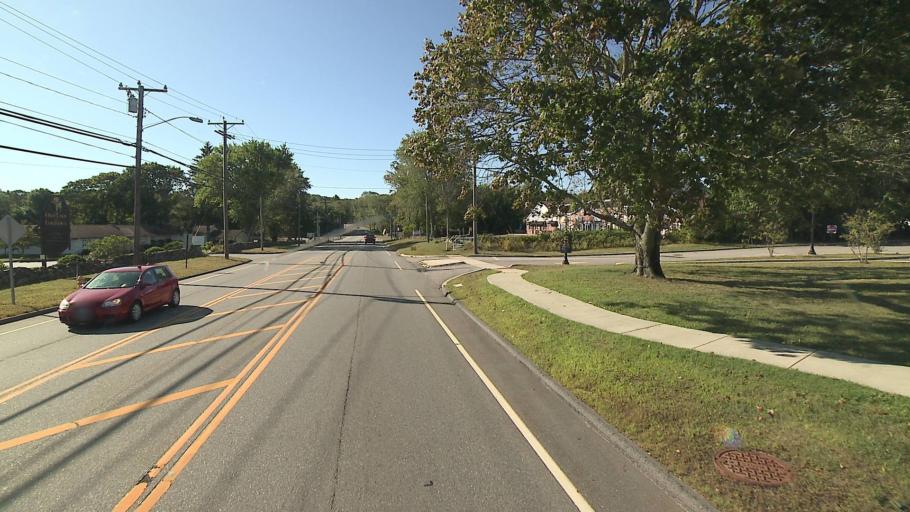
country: US
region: Connecticut
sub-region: New London County
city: Gales Ferry
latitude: 41.4276
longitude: -72.0821
